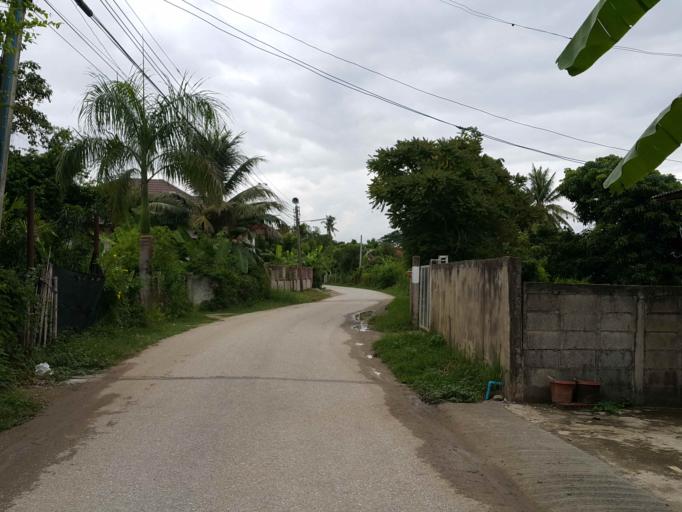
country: TH
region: Chiang Mai
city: San Sai
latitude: 18.8261
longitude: 99.0619
